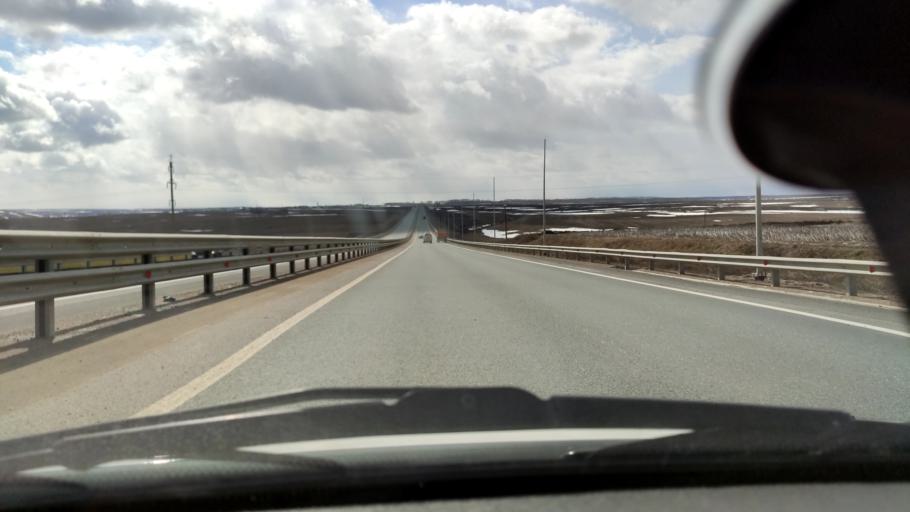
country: RU
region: Bashkortostan
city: Tolbazy
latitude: 54.2331
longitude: 55.8817
